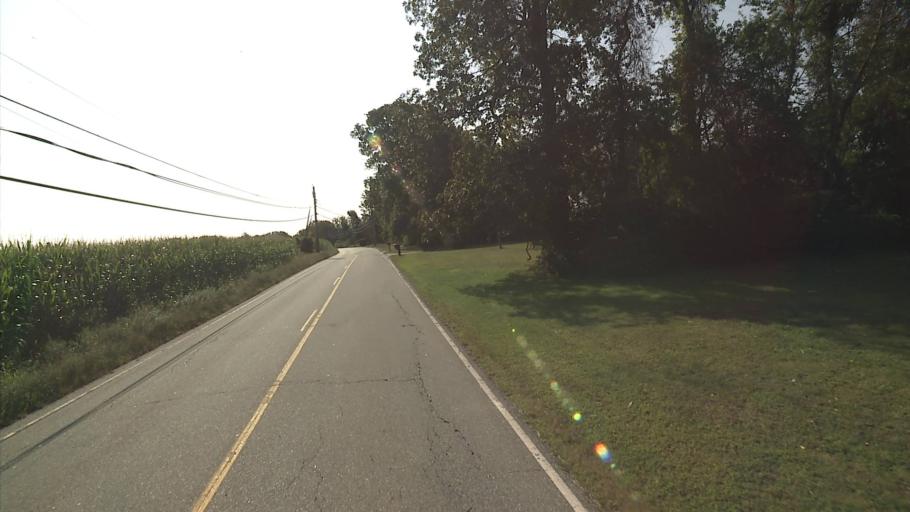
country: US
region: Connecticut
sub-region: Windham County
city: South Windham
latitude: 41.6085
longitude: -72.1758
